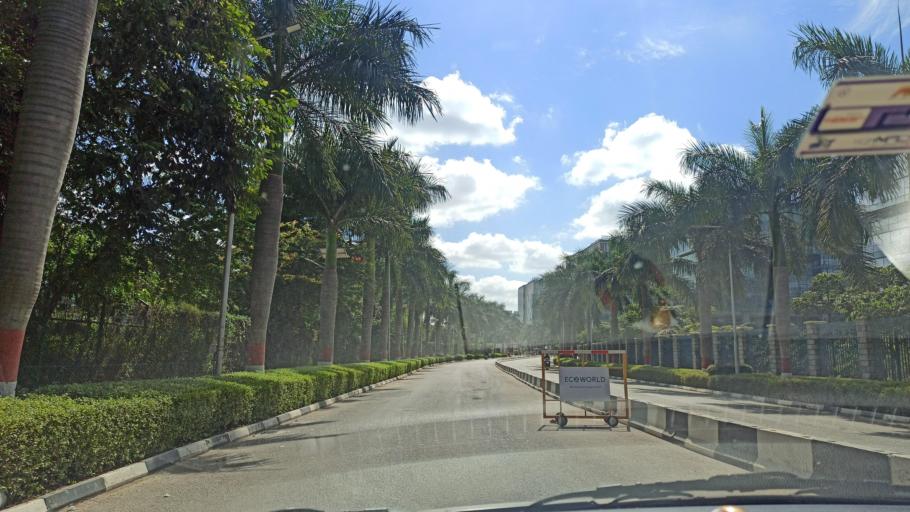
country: IN
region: Karnataka
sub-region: Bangalore Urban
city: Bangalore
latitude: 12.9238
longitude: 77.6858
